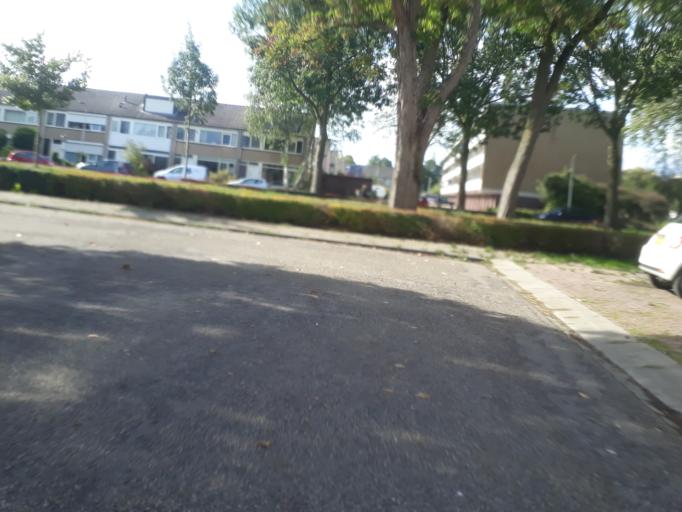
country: NL
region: Gelderland
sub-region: Gemeente Zevenaar
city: Zevenaar
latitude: 51.9300
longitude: 6.0616
